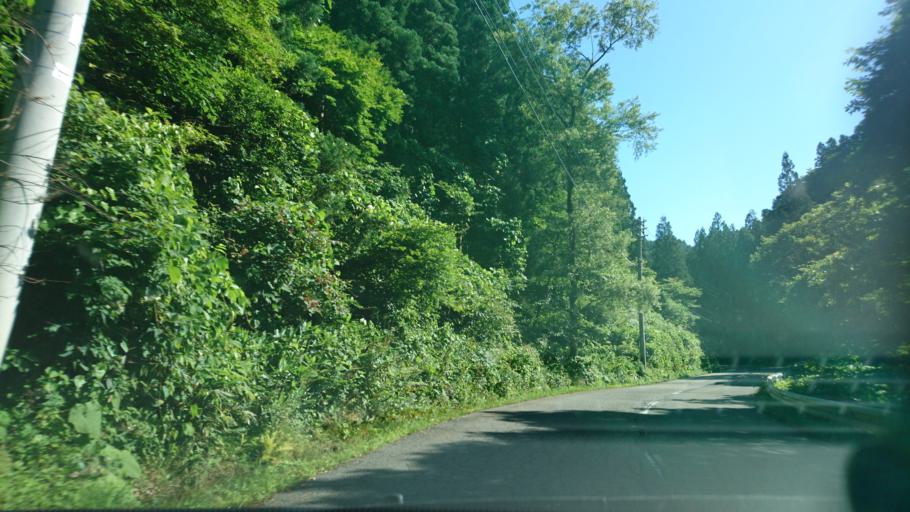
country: JP
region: Akita
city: Kakunodatemachi
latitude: 39.7146
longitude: 140.6182
